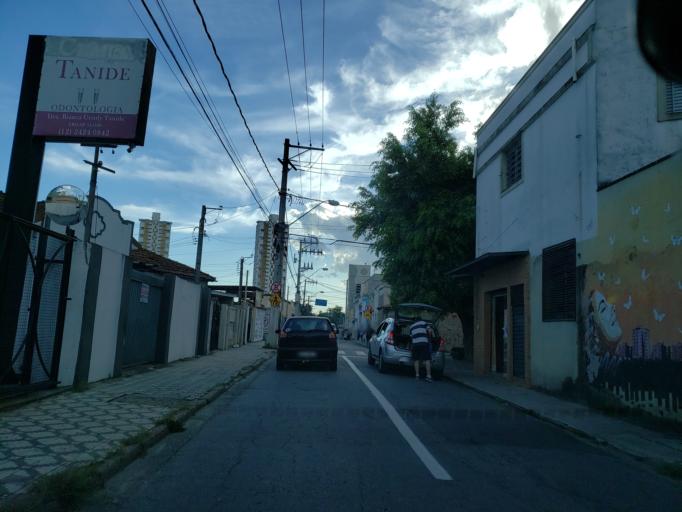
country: BR
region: Sao Paulo
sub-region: Taubate
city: Taubate
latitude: -23.0336
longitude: -45.5637
